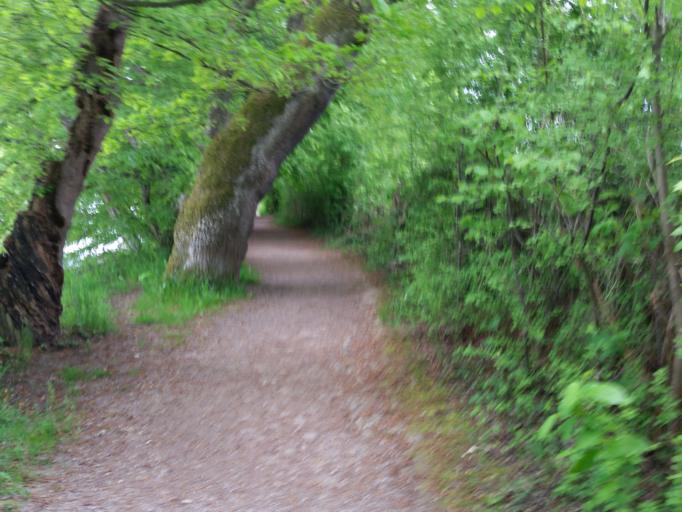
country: CH
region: Thurgau
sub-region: Kreuzlingen District
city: Guttingen
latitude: 47.6017
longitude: 9.3126
